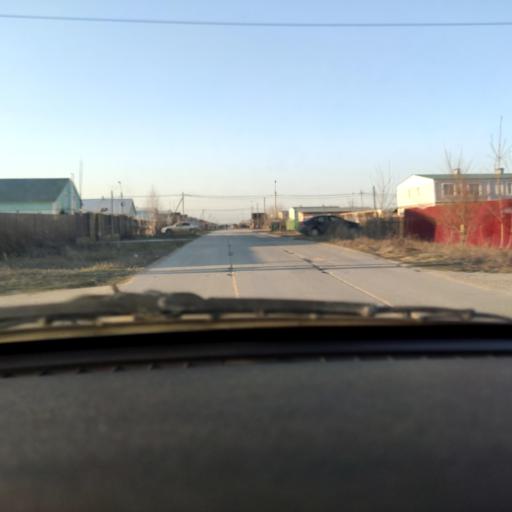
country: RU
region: Samara
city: Podstepki
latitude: 53.5705
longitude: 49.1189
